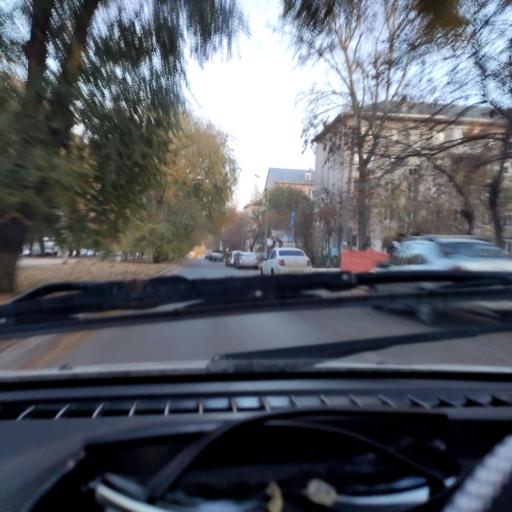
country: RU
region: Samara
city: Tol'yatti
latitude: 53.5161
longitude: 49.4205
